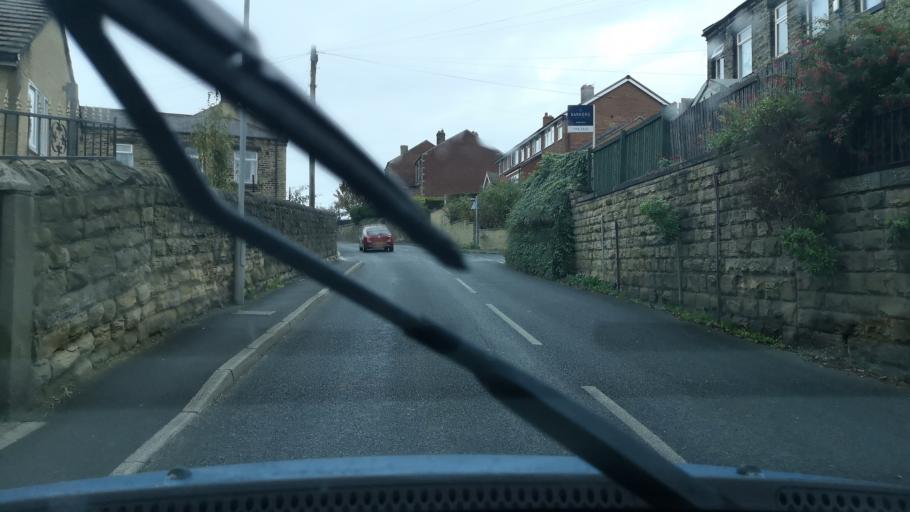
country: GB
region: England
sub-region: Kirklees
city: Heckmondwike
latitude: 53.7117
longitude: -1.6739
